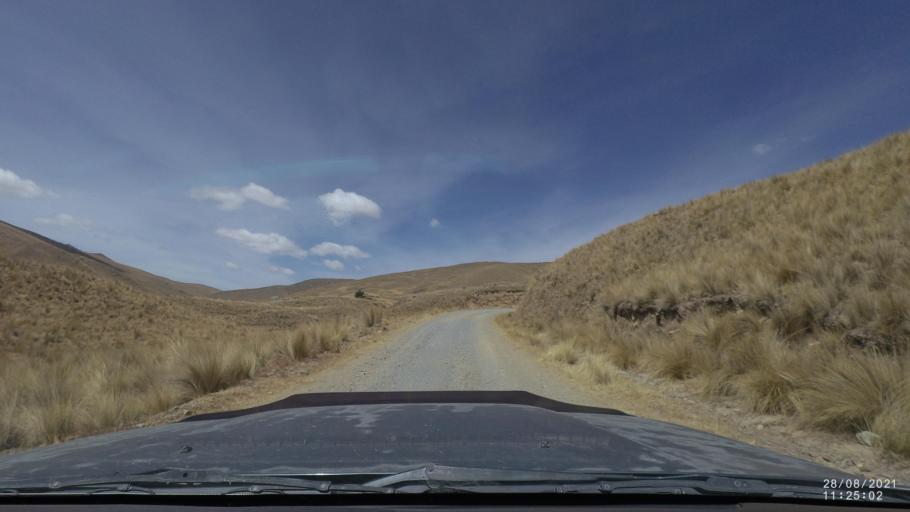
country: BO
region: Cochabamba
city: Sipe Sipe
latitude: -17.1704
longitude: -66.3525
